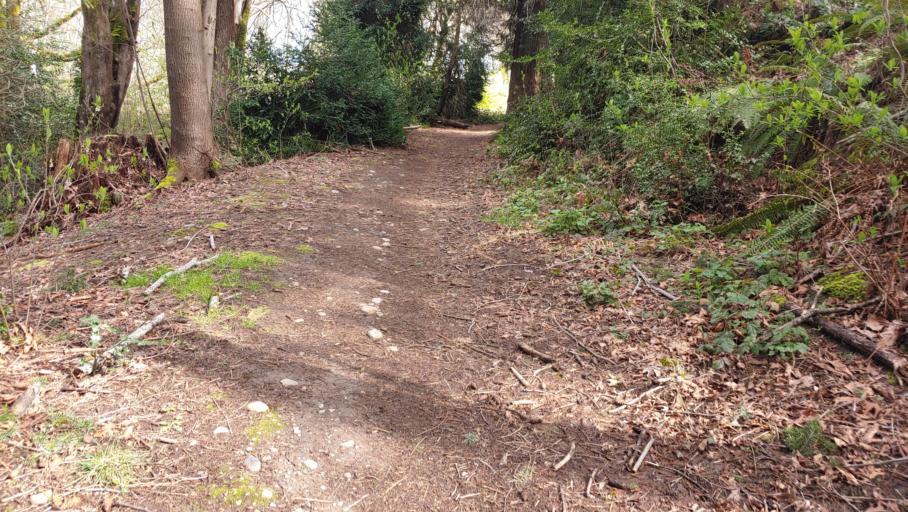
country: US
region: Washington
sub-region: King County
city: Des Moines
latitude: 47.4122
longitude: -122.3112
